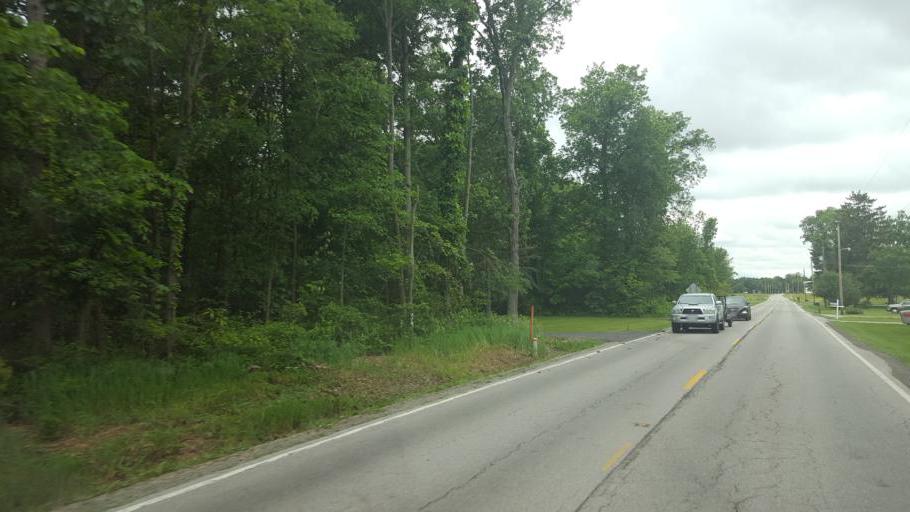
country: US
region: Ohio
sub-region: Crawford County
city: Bucyrus
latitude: 40.7661
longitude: -82.9213
